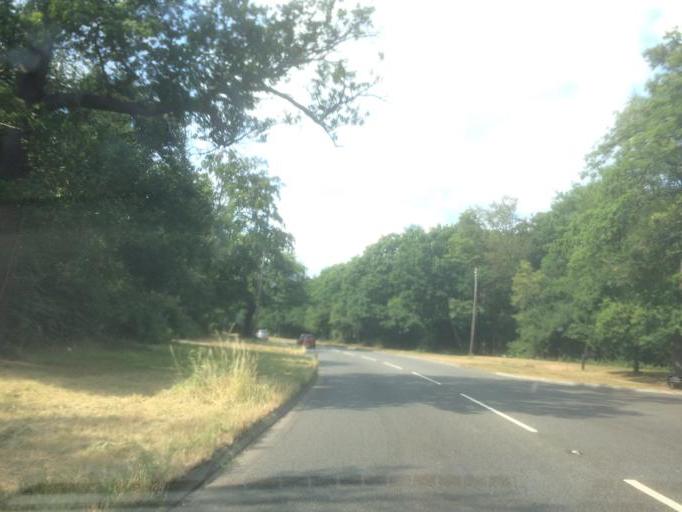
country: GB
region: England
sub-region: Buckinghamshire
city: Farnham Royal
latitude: 51.5680
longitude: -0.6178
